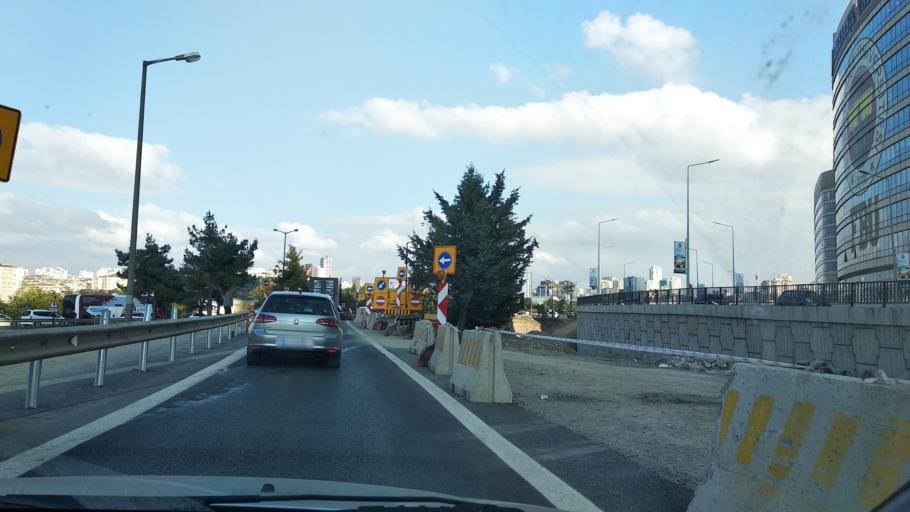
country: TR
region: Istanbul
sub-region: Atasehir
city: Atasehir
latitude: 40.9949
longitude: 29.1193
